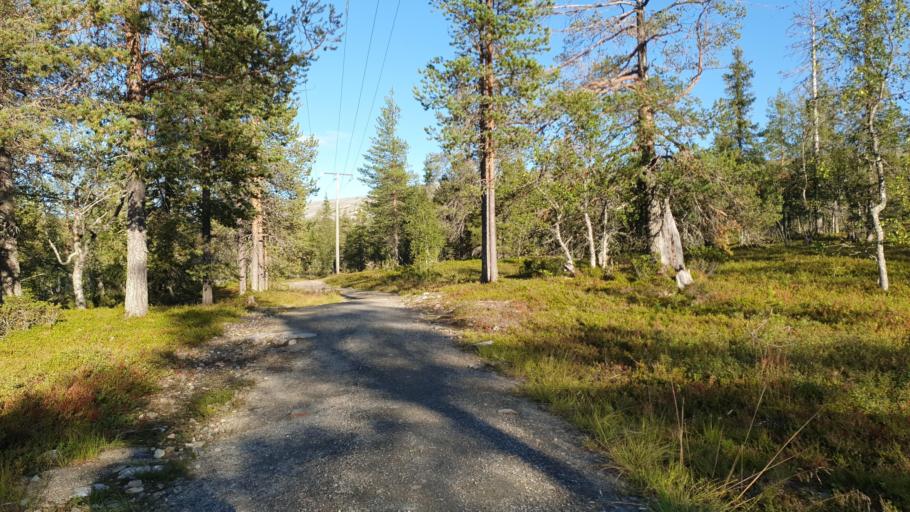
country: FI
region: Lapland
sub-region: Tunturi-Lappi
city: Kolari
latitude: 67.5832
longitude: 24.2116
